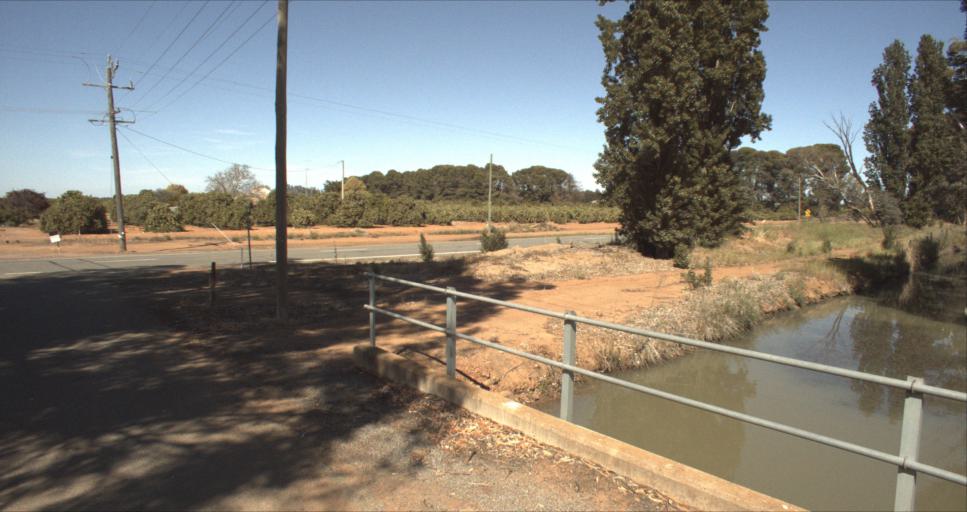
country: AU
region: New South Wales
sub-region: Leeton
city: Leeton
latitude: -34.5435
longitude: 146.3438
